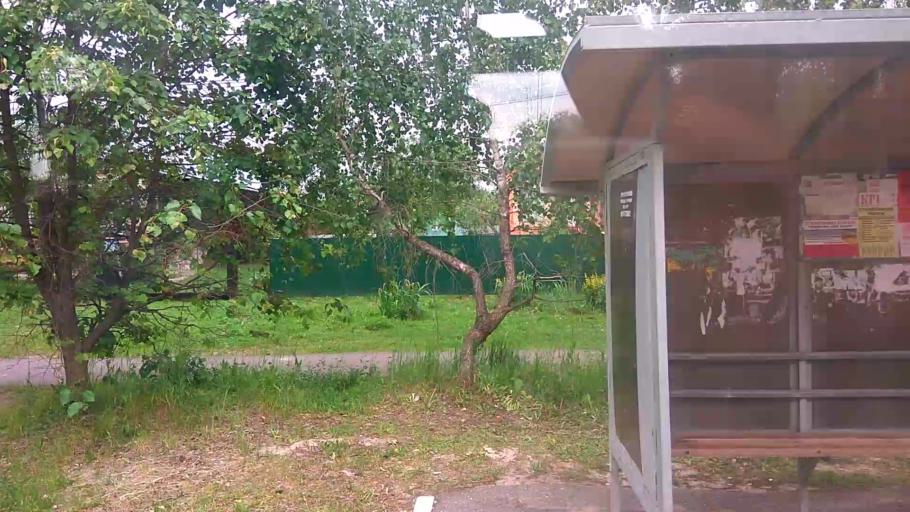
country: RU
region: Moskovskaya
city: Lukhovitsy
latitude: 54.9408
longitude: 39.0165
